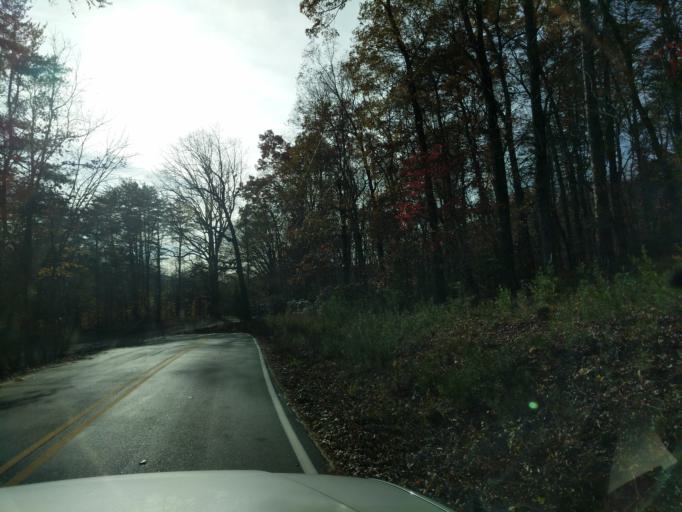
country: US
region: North Carolina
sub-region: Polk County
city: Columbus
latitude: 35.2548
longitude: -82.2308
